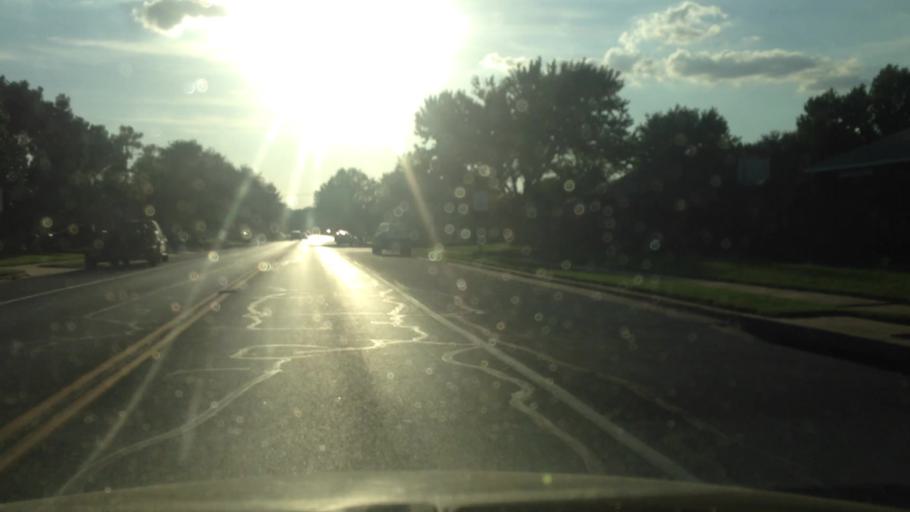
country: US
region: Texas
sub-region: Tarrant County
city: Watauga
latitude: 32.8746
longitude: -97.2404
